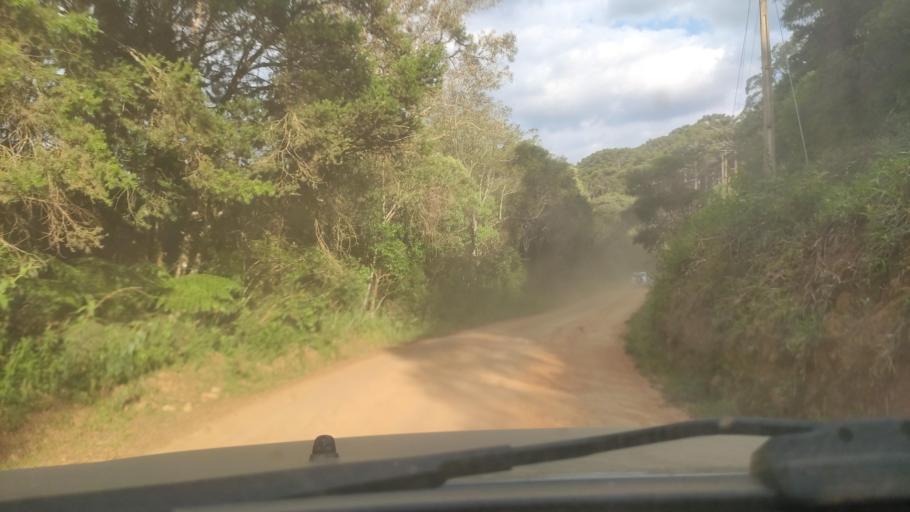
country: BR
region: Minas Gerais
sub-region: Cambui
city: Cambui
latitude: -22.7556
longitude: -45.9478
